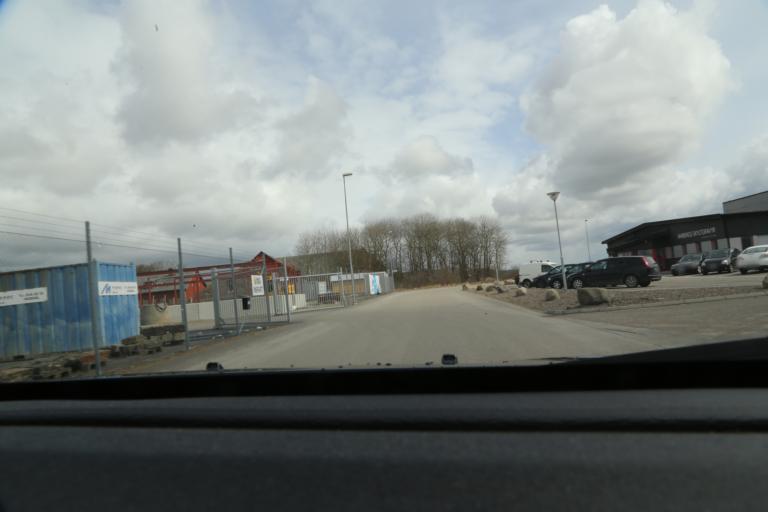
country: SE
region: Halland
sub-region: Varbergs Kommun
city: Varberg
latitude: 57.1223
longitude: 12.3004
